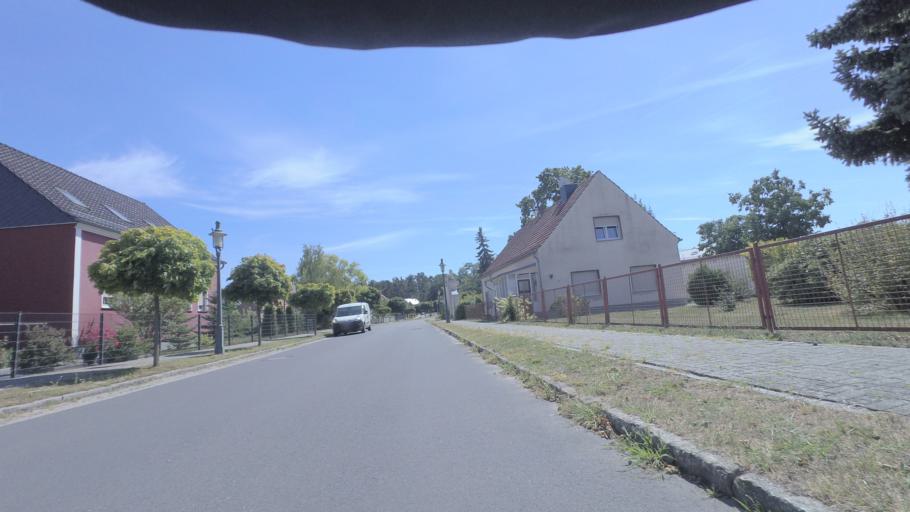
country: DE
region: Brandenburg
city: Trebbin
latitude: 52.2124
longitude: 13.1467
